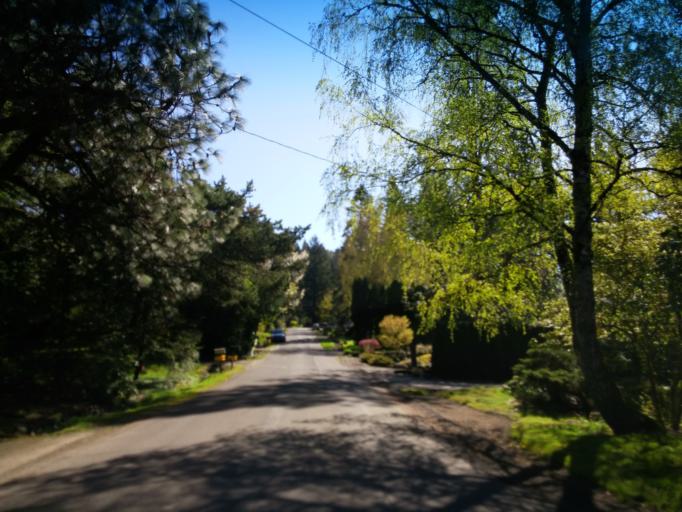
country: US
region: Oregon
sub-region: Washington County
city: West Haven
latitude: 45.5173
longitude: -122.7721
